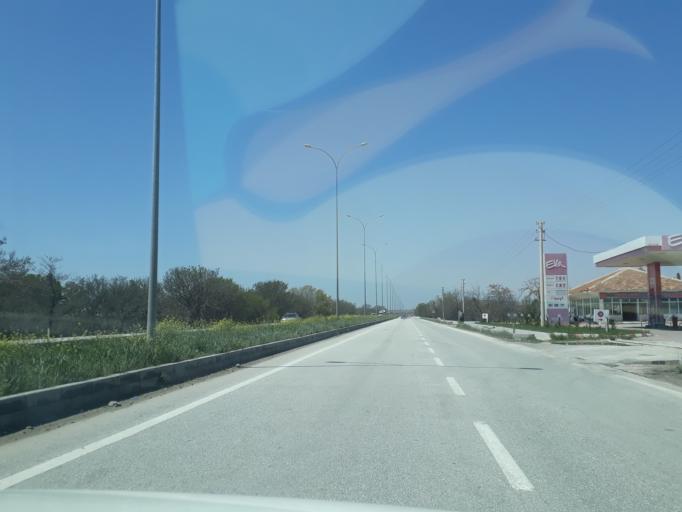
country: TR
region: Konya
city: Karapinar
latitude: 37.7141
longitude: 33.5254
